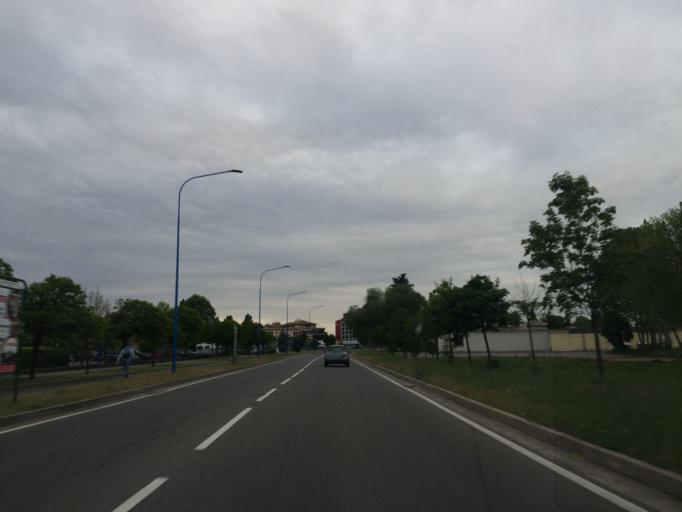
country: IT
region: Lombardy
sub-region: Provincia di Brescia
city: Buffalora-Bettole
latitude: 45.5237
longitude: 10.2589
